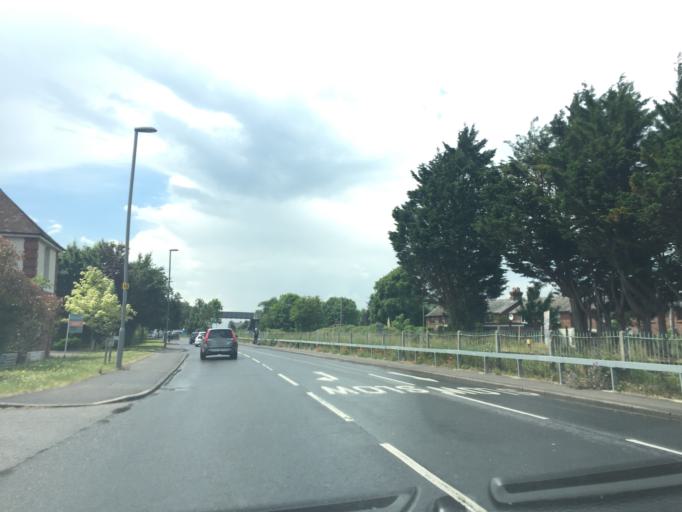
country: GB
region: England
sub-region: Dorset
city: Wool
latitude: 50.6812
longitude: -2.2233
